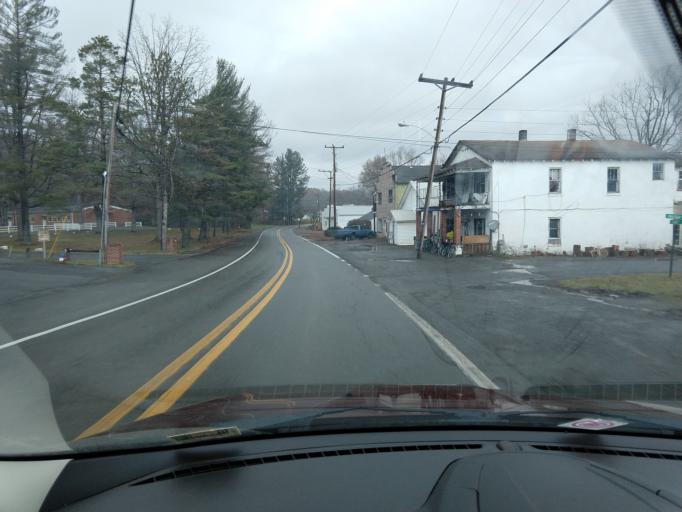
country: US
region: West Virginia
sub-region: Greenbrier County
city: Rainelle
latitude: 37.9642
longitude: -80.6870
